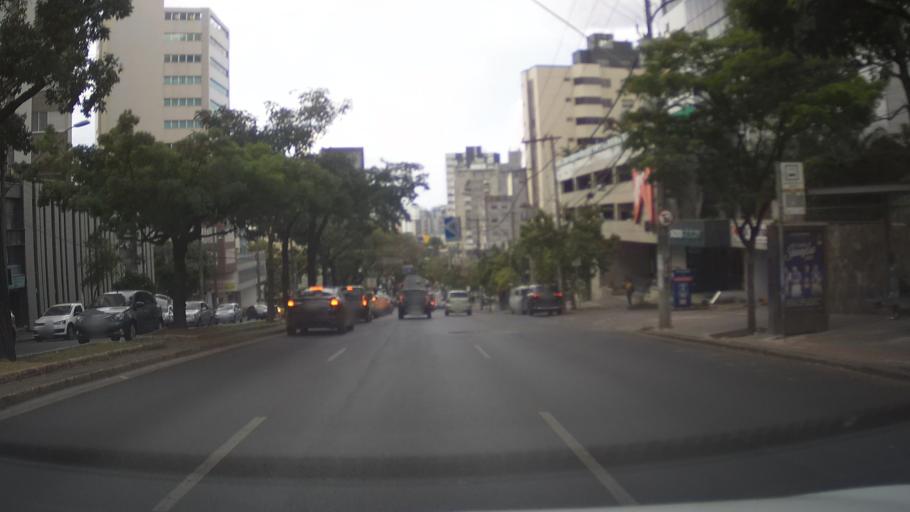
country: BR
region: Minas Gerais
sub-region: Belo Horizonte
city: Belo Horizonte
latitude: -19.9316
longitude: -43.9239
